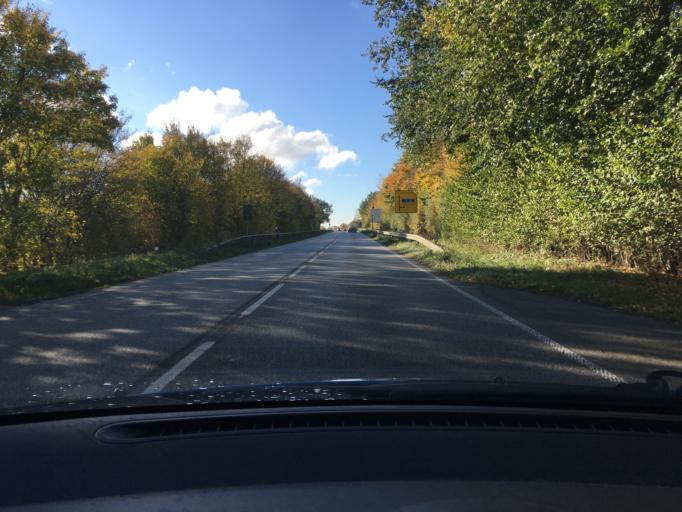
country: DE
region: Schleswig-Holstein
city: Busdorf
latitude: 54.4868
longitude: 9.5527
